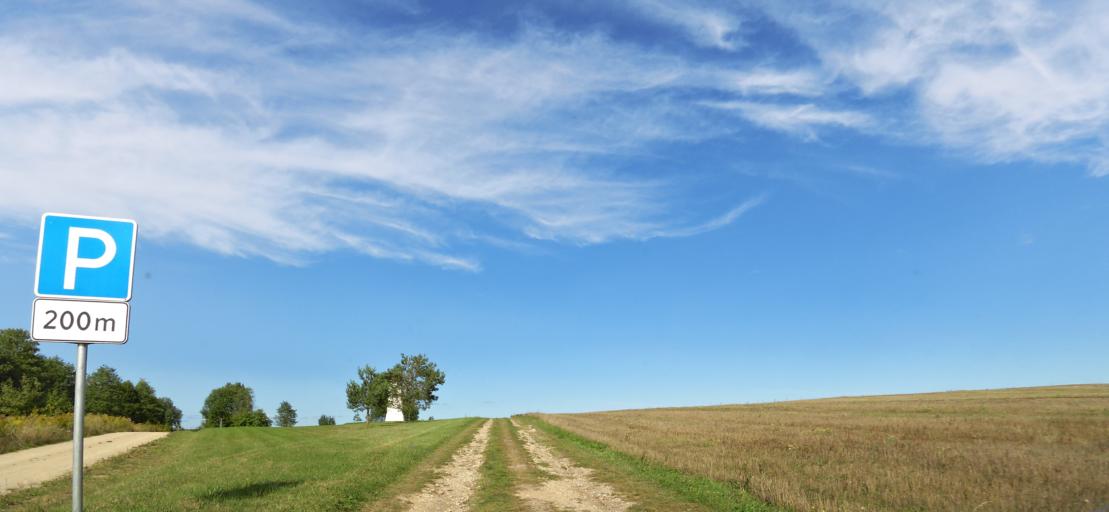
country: LT
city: Skaidiskes
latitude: 54.4594
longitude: 25.4782
